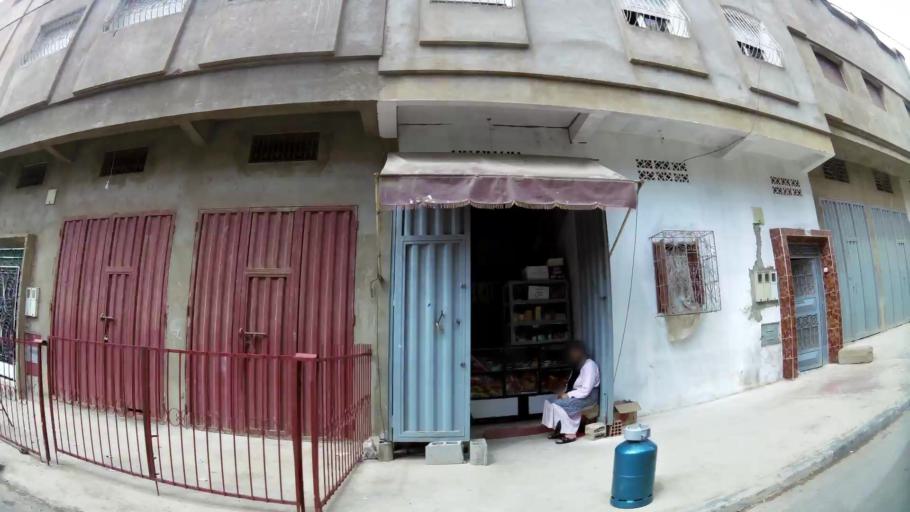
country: MA
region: Rabat-Sale-Zemmour-Zaer
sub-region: Khemisset
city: Tiflet
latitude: 33.8885
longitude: -6.3247
